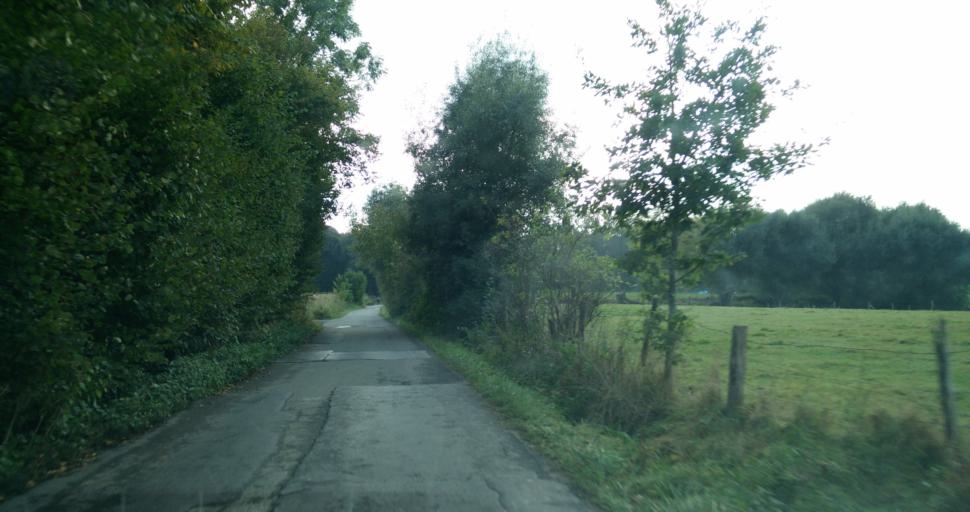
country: BE
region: Flanders
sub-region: Provincie Vlaams-Brabant
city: Halle
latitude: 50.7309
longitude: 4.2584
